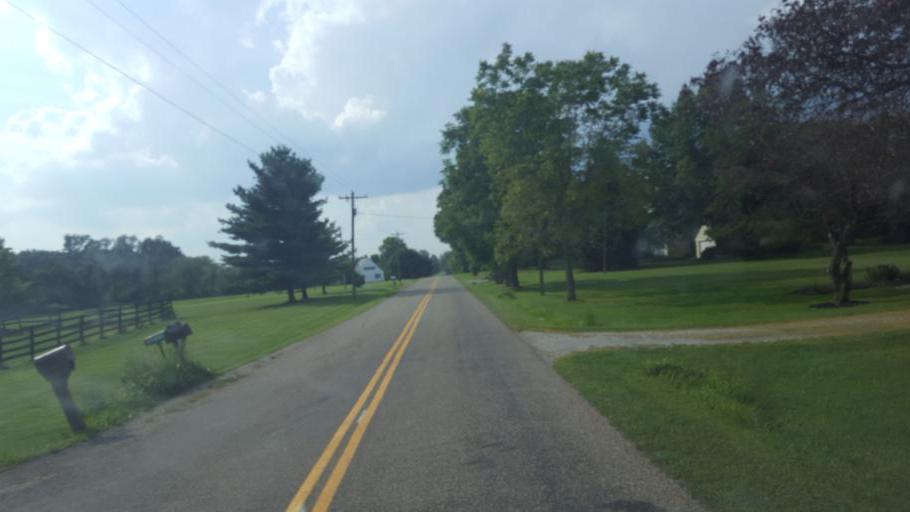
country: US
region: Ohio
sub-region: Knox County
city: Gambier
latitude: 40.3527
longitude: -82.4251
